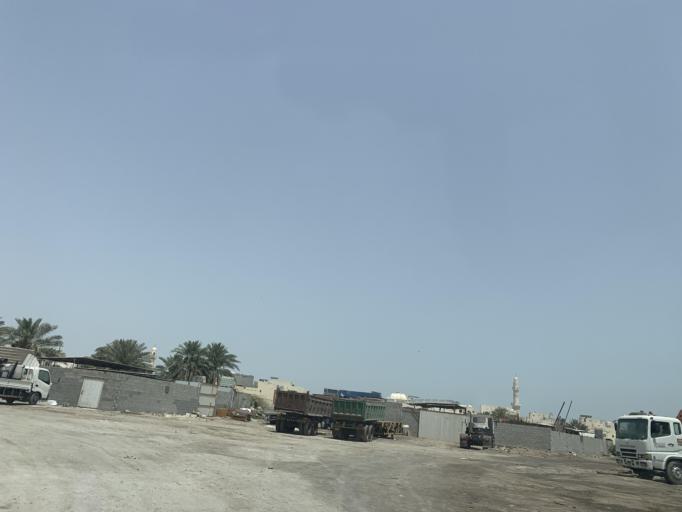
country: BH
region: Northern
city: Sitrah
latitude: 26.1371
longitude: 50.5935
